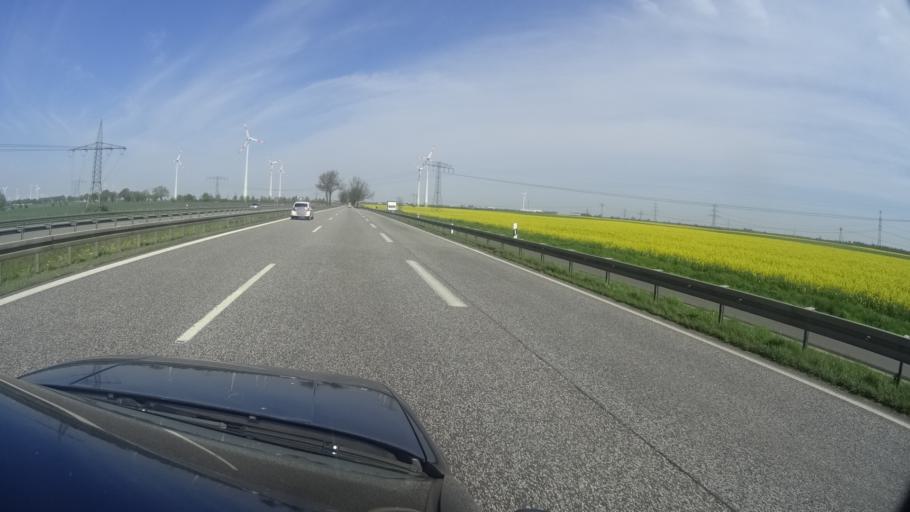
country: DE
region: Brandenburg
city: Nauen
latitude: 52.5794
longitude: 12.9057
